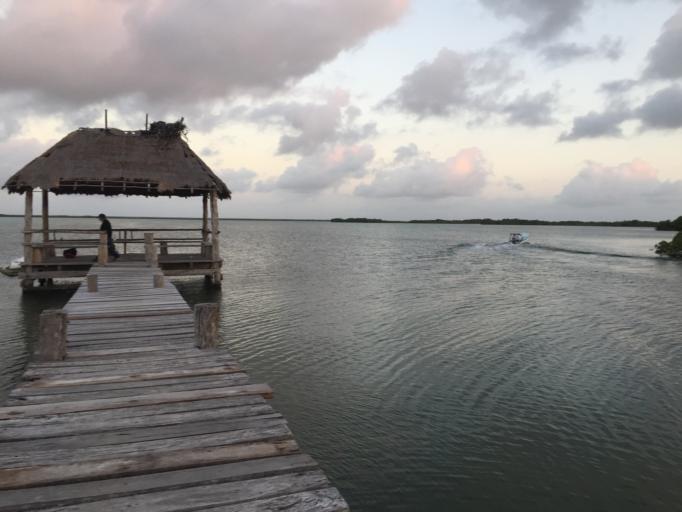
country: MX
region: Quintana Roo
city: Tulum
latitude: 19.8038
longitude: -87.4812
